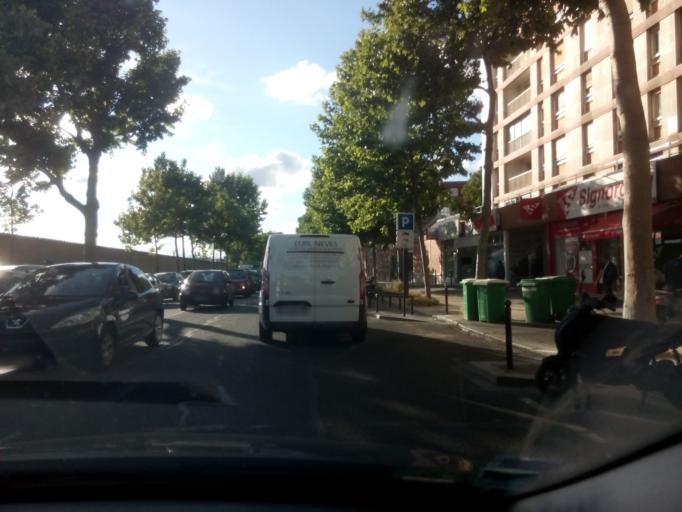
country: FR
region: Ile-de-France
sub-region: Departement du Val-de-Marne
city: Charenton-le-Pont
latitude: 48.8329
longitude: 2.3962
